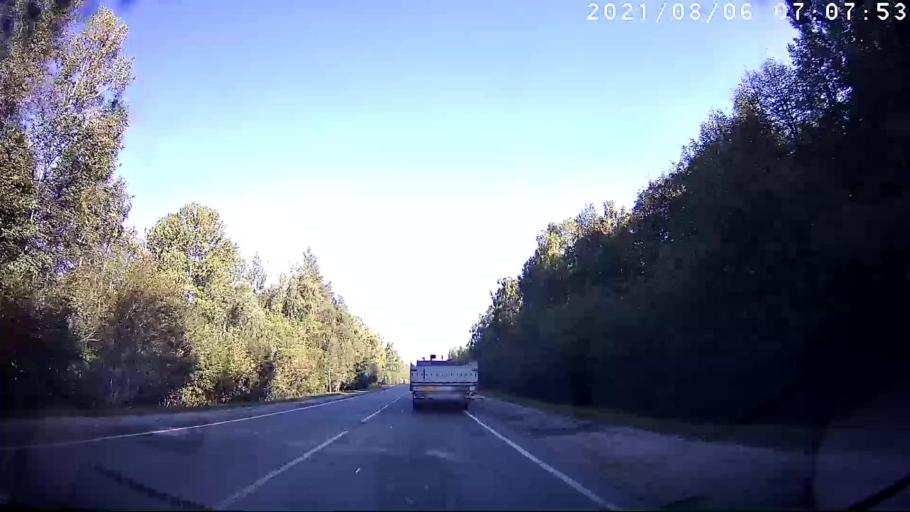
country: RU
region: Mariy-El
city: Yoshkar-Ola
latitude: 56.5661
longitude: 47.9758
